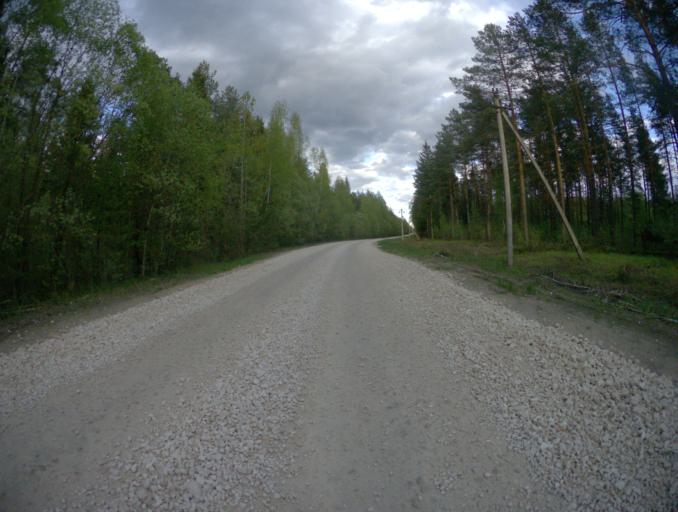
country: RU
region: Vladimir
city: Gusevskiy
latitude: 55.7216
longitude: 40.5742
